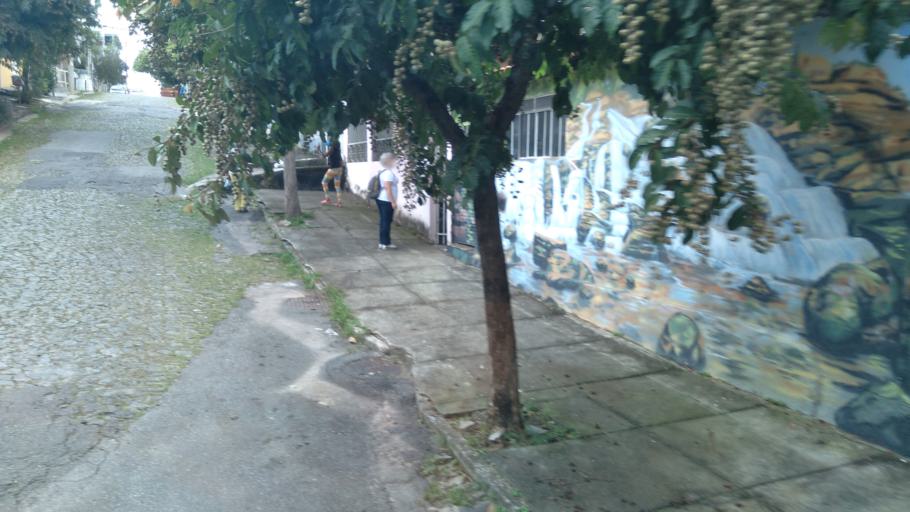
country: BR
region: Minas Gerais
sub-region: Belo Horizonte
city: Belo Horizonte
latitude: -19.8867
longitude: -43.8988
